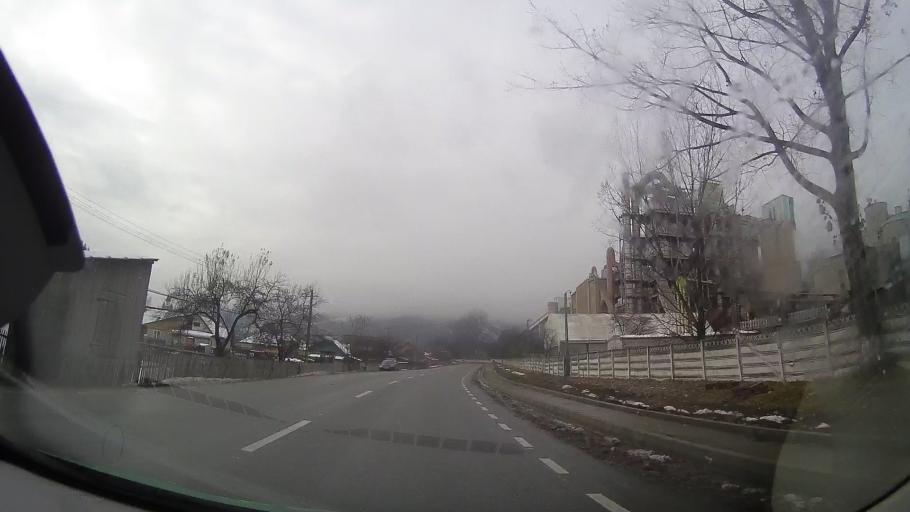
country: RO
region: Neamt
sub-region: Comuna Tasca
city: Tasca
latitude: 46.8961
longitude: 26.0314
